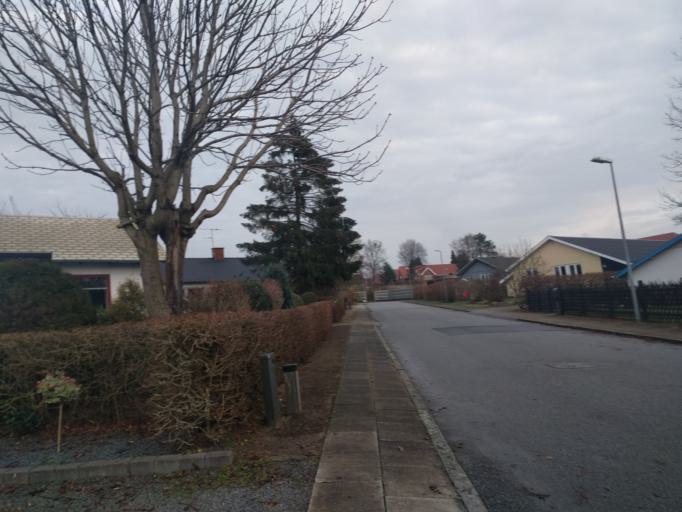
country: DK
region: Central Jutland
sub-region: Viborg Kommune
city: Viborg
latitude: 56.4499
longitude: 9.3864
